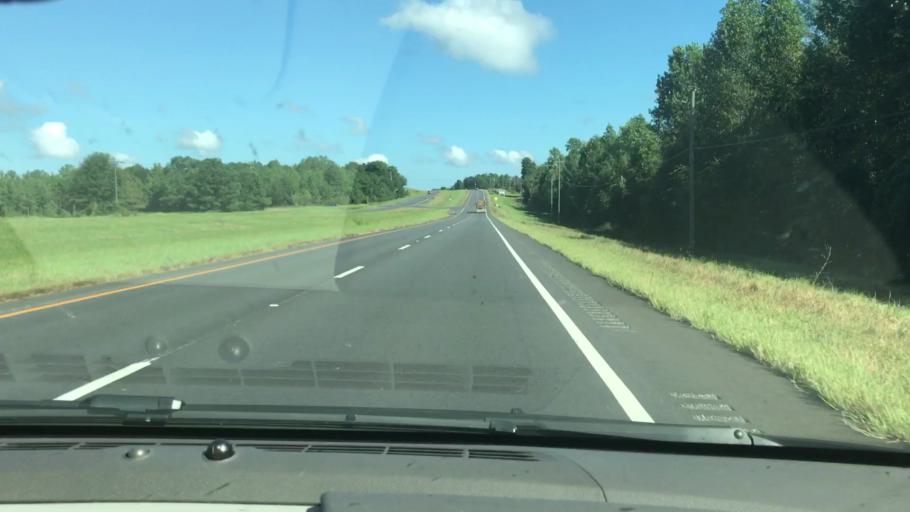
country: US
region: Alabama
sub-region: Barbour County
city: Eufaula
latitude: 32.0227
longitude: -85.1187
